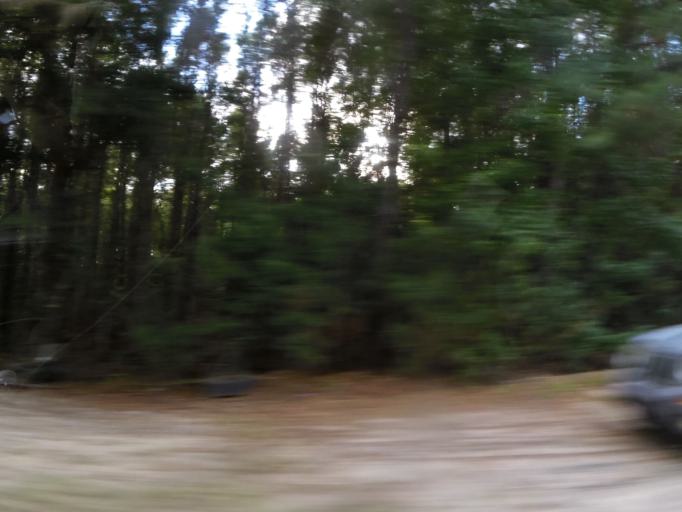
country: US
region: Georgia
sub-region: Liberty County
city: Midway
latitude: 31.6718
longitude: -81.4019
